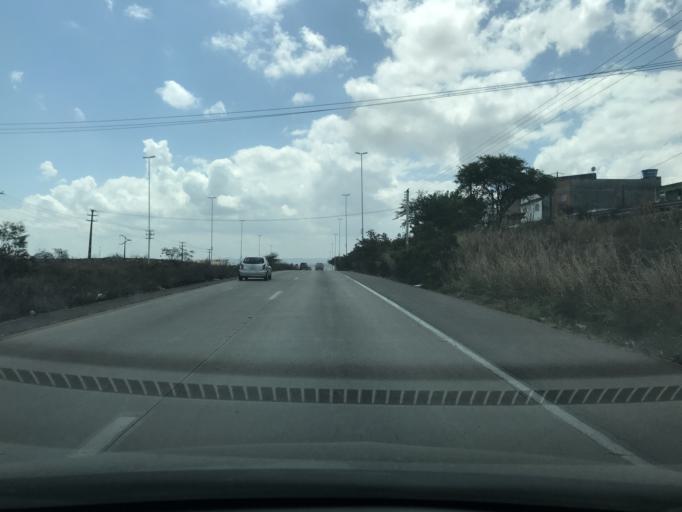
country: BR
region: Pernambuco
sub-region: Caruaru
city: Caruaru
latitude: -8.3025
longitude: -35.9786
